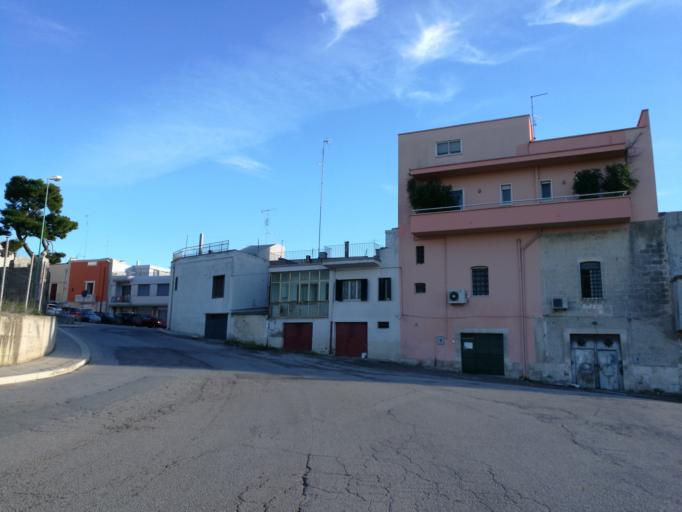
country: IT
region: Apulia
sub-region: Provincia di Bari
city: Adelfia
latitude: 41.0043
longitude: 16.8740
